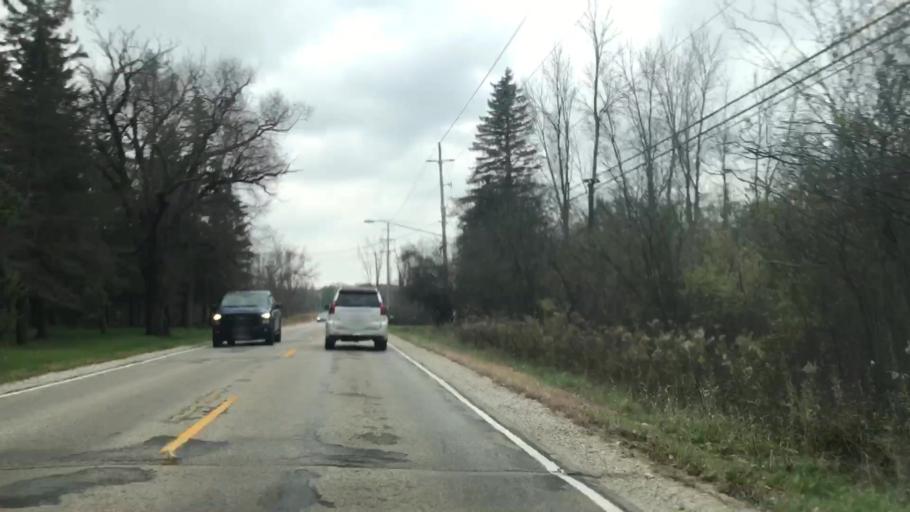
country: US
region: Wisconsin
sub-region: Waukesha County
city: Menomonee Falls
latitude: 43.2009
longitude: -88.1427
